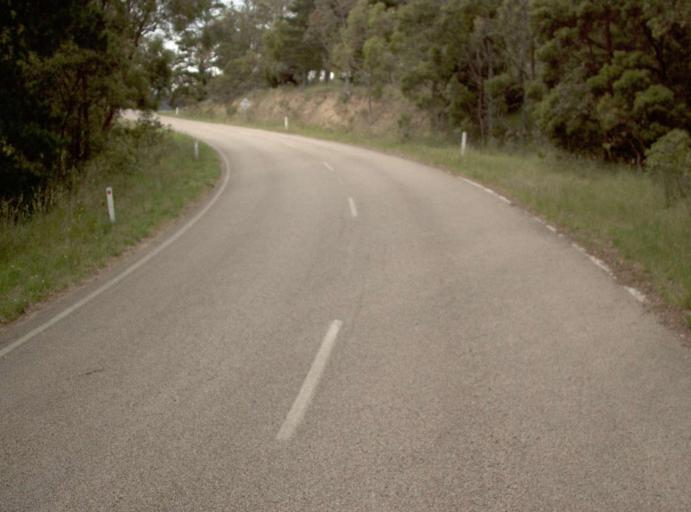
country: AU
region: Victoria
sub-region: East Gippsland
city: Bairnsdale
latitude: -37.5724
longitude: 147.1868
